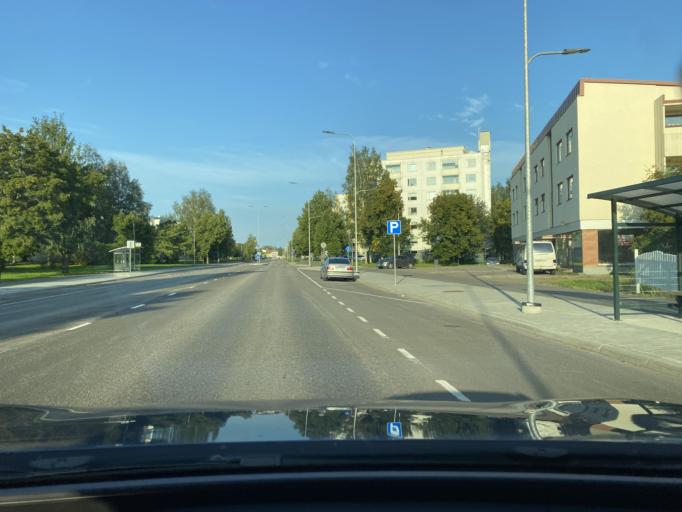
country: FI
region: Kymenlaakso
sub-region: Kouvola
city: Kouvola
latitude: 60.9043
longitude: 26.6101
